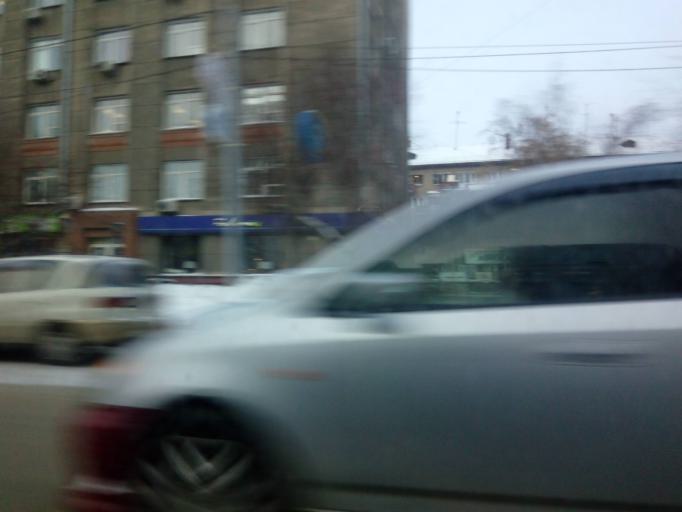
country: RU
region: Novosibirsk
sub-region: Novosibirskiy Rayon
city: Novosibirsk
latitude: 55.0314
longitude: 82.9132
